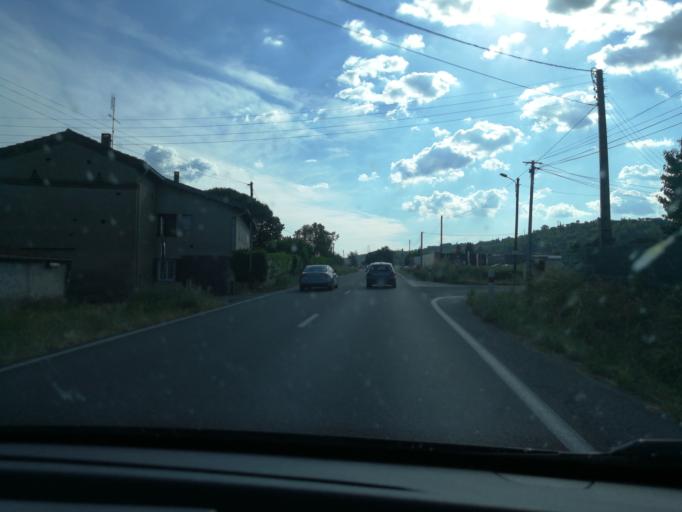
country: FR
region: Midi-Pyrenees
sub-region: Departement du Tarn
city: Cagnac-les-Mines
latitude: 43.9617
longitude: 2.1703
